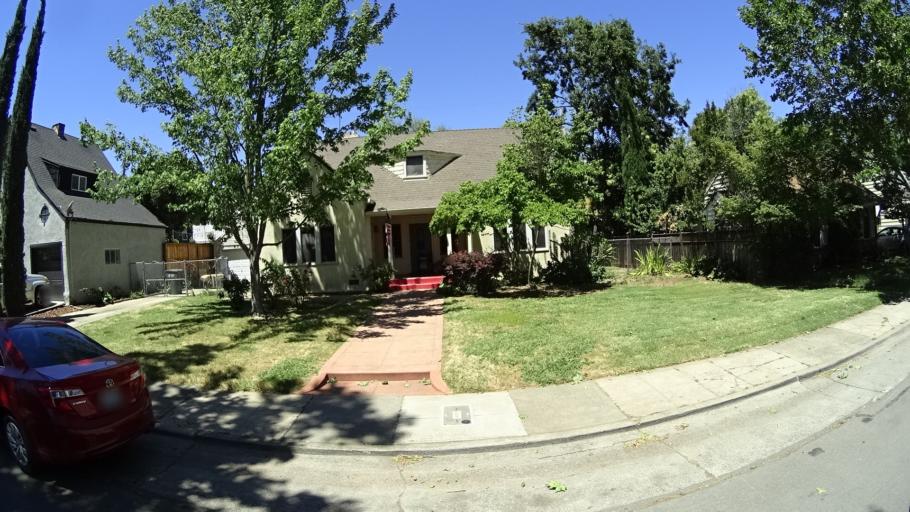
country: US
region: California
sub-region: Sacramento County
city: Sacramento
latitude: 38.5731
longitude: -121.4508
